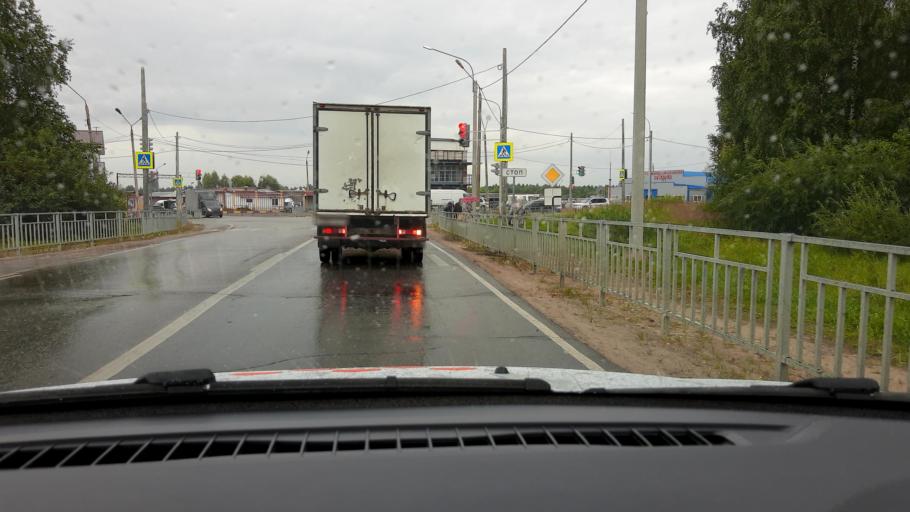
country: RU
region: Nizjnij Novgorod
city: Satis
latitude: 54.9389
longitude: 43.2600
